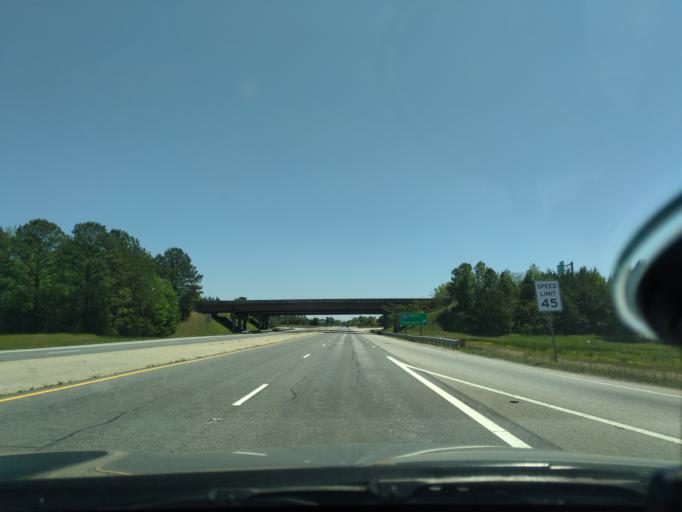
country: US
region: Virginia
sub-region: Prince George County
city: Prince George
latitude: 37.1938
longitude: -77.3291
